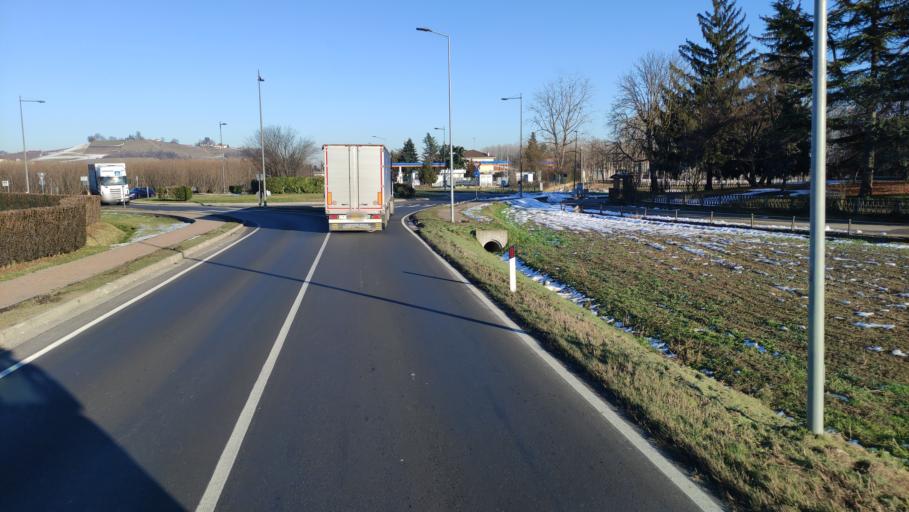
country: IT
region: Piedmont
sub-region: Provincia di Cuneo
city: Borgo
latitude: 44.7040
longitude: 7.9833
